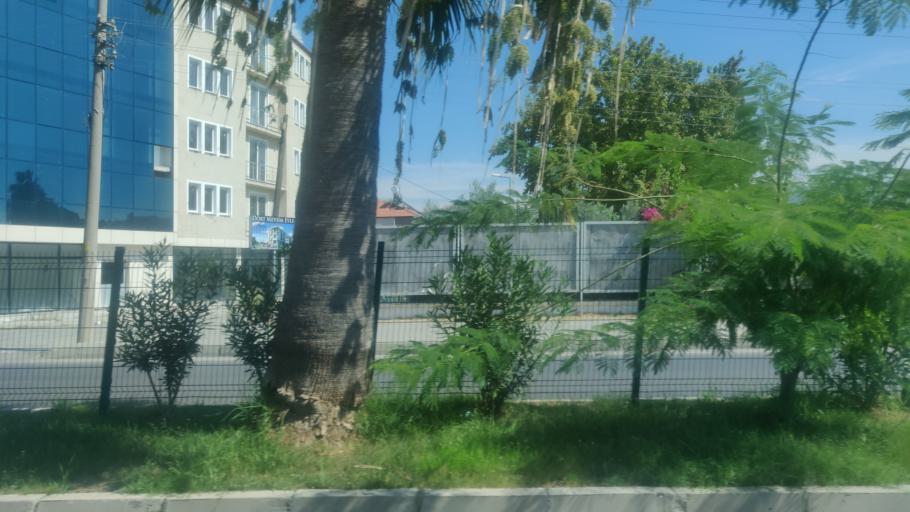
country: TR
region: Mugla
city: Dalaman
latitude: 36.7736
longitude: 28.8000
